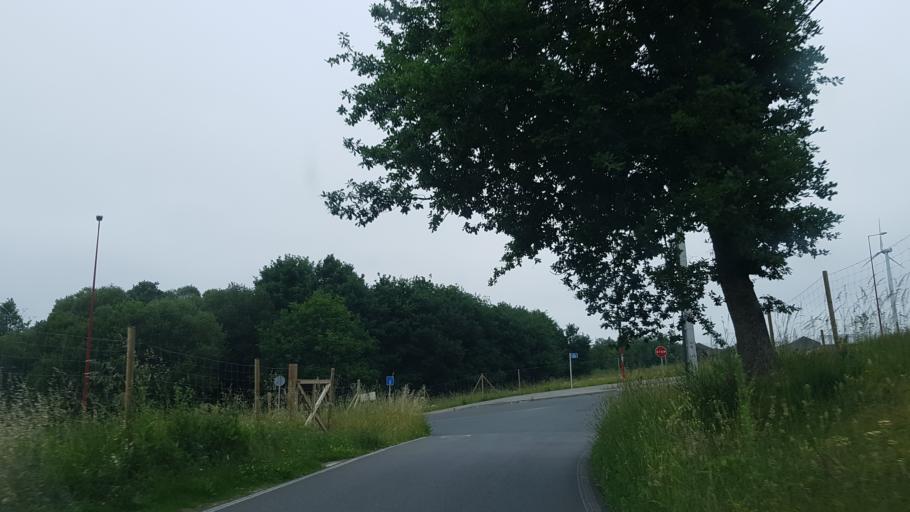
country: ES
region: Galicia
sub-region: Provincia de Lugo
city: Lugo
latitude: 43.0383
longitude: -7.5590
